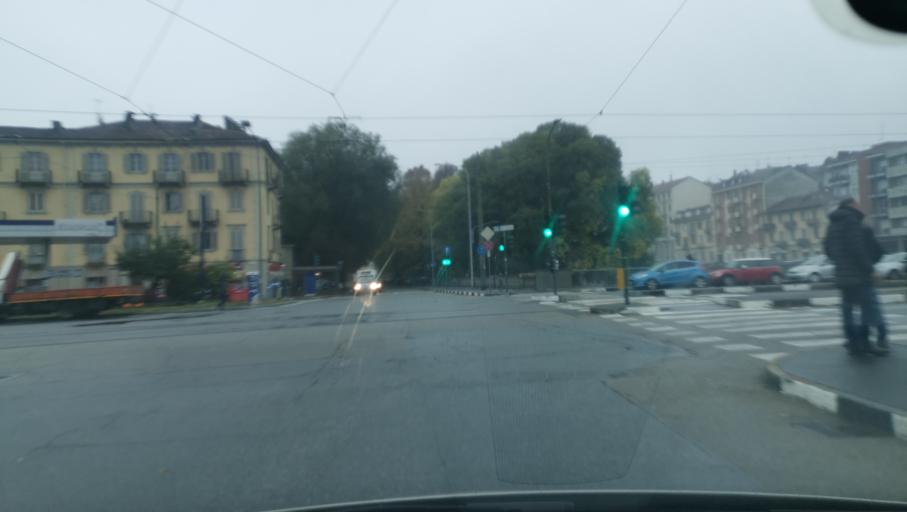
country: IT
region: Piedmont
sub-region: Provincia di Torino
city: Turin
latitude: 45.0761
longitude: 7.6922
